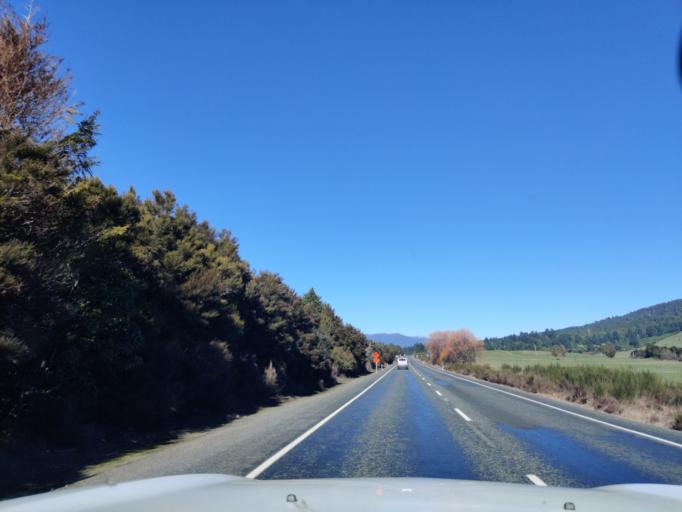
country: NZ
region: Waikato
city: Turangi
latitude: -39.0123
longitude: 175.8072
